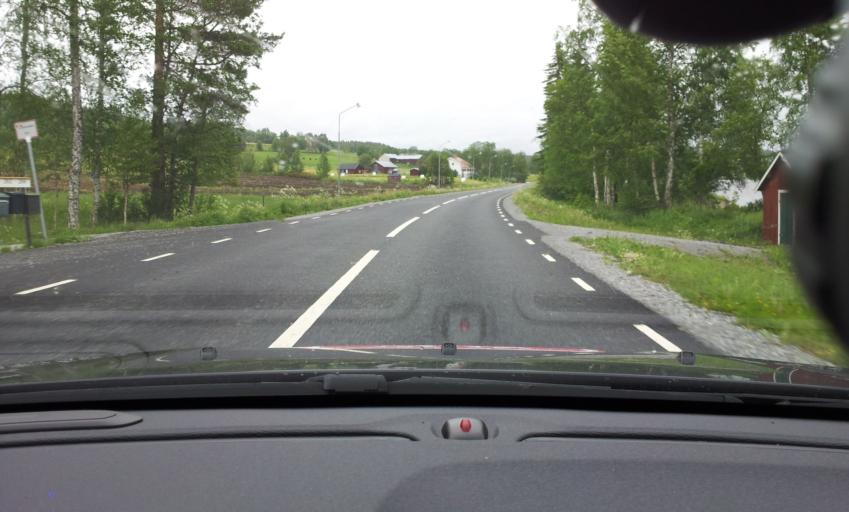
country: SE
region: Jaemtland
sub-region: OEstersunds Kommun
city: Lit
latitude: 63.7434
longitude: 14.8235
